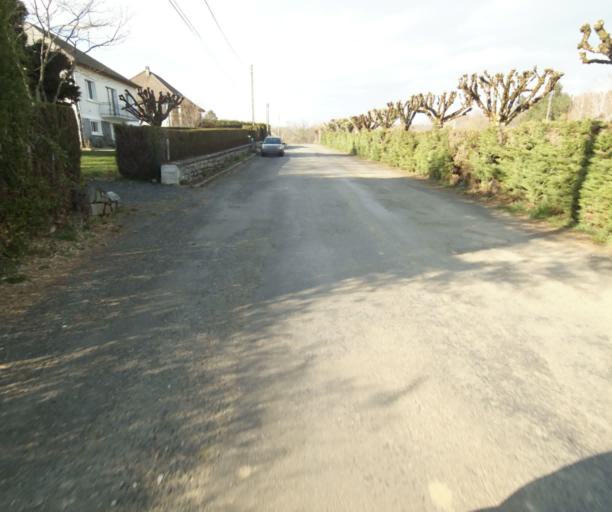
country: FR
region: Limousin
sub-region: Departement de la Correze
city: Saint-Clement
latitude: 45.3489
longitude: 1.6448
